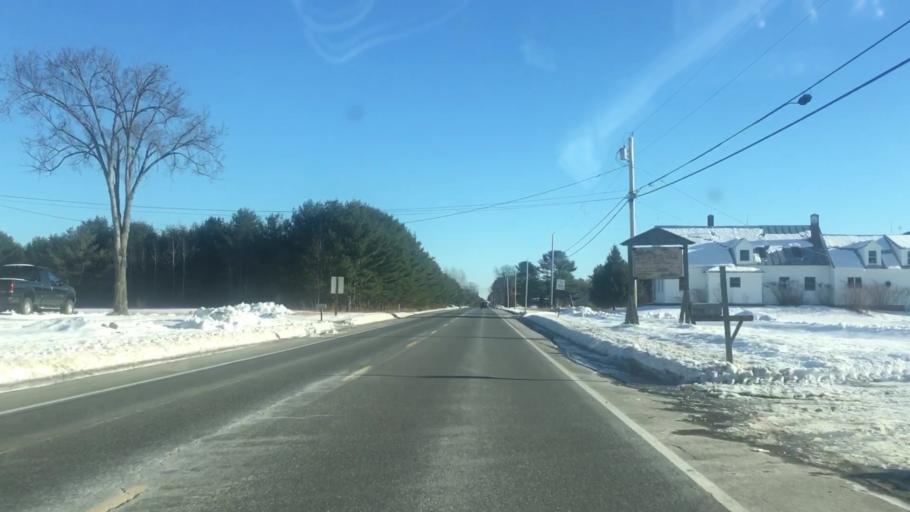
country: US
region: Maine
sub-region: Somerset County
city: Norridgewock
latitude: 44.7075
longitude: -69.7748
